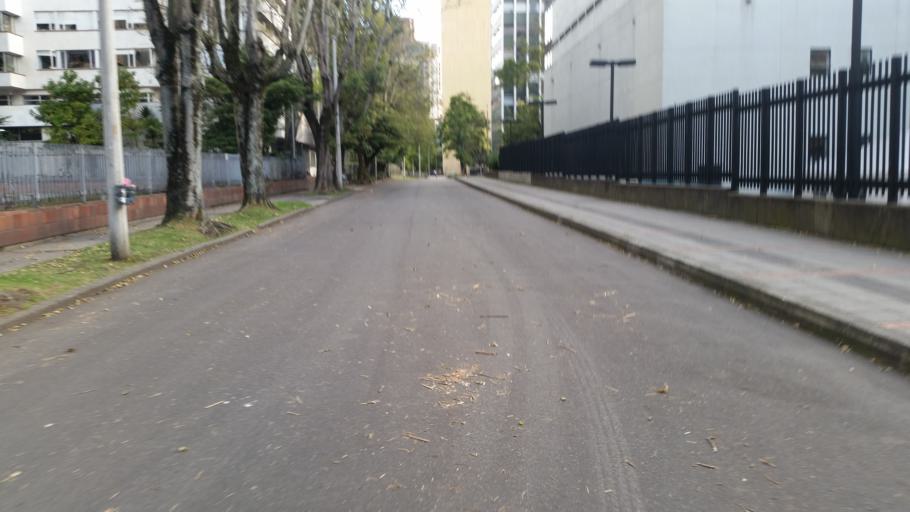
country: CO
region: Bogota D.C.
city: Bogota
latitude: 4.6257
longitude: -74.0665
